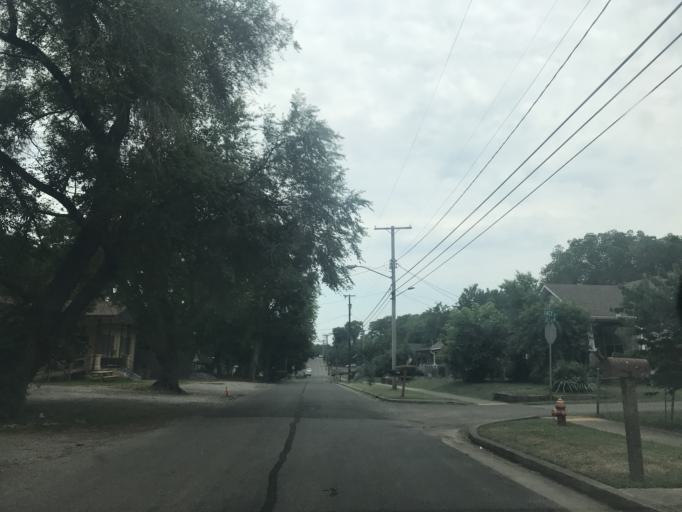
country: US
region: Tennessee
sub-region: Davidson County
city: Nashville
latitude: 36.1831
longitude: -86.8159
